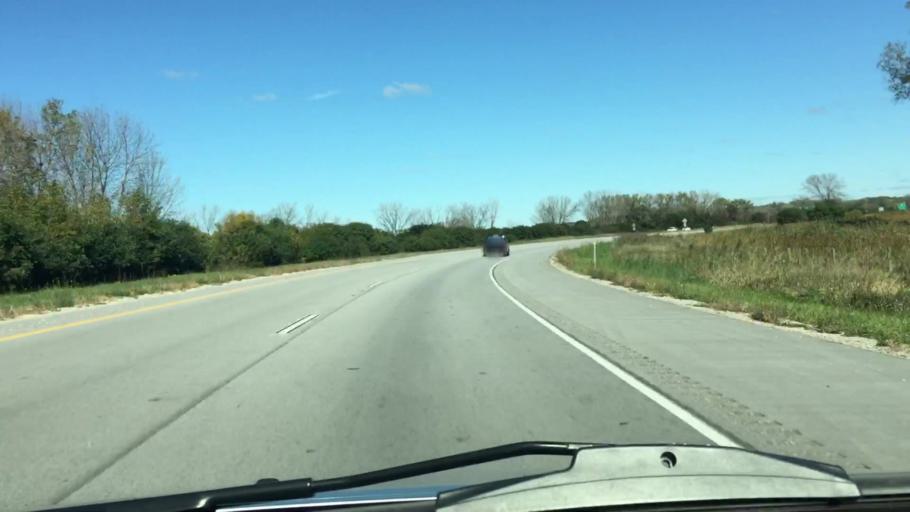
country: US
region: Wisconsin
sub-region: Waukesha County
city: Pewaukee
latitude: 43.0497
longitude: -88.2500
